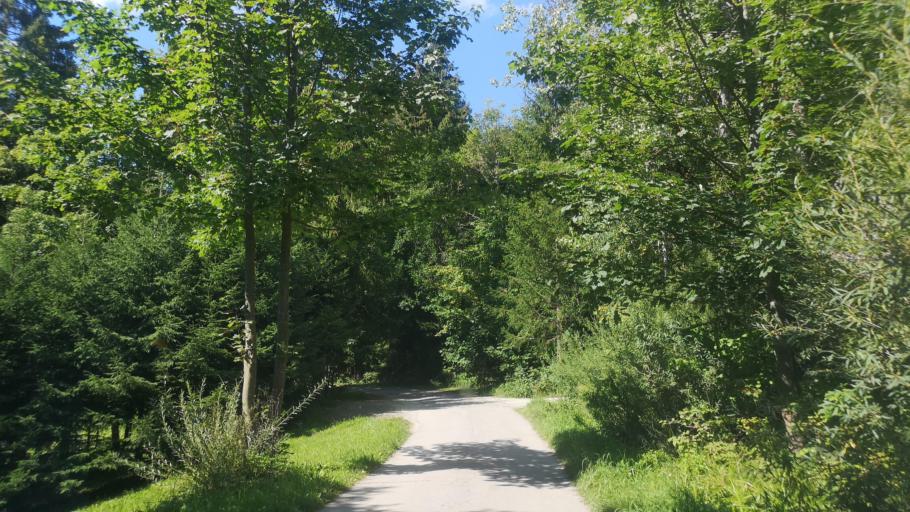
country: SK
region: Zilinsky
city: Oravska Lesna
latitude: 49.2949
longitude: 19.1391
